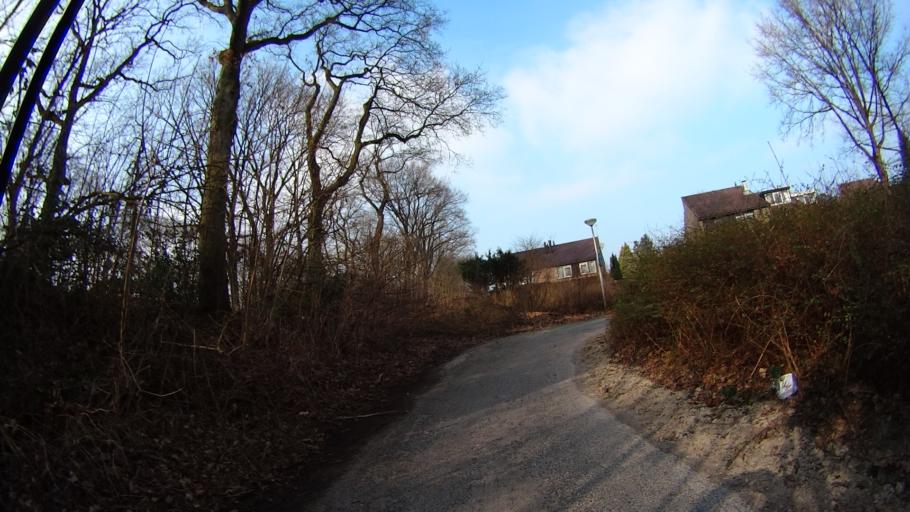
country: NL
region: Drenthe
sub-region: Gemeente Emmen
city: Emmen
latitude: 52.7616
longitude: 6.8904
